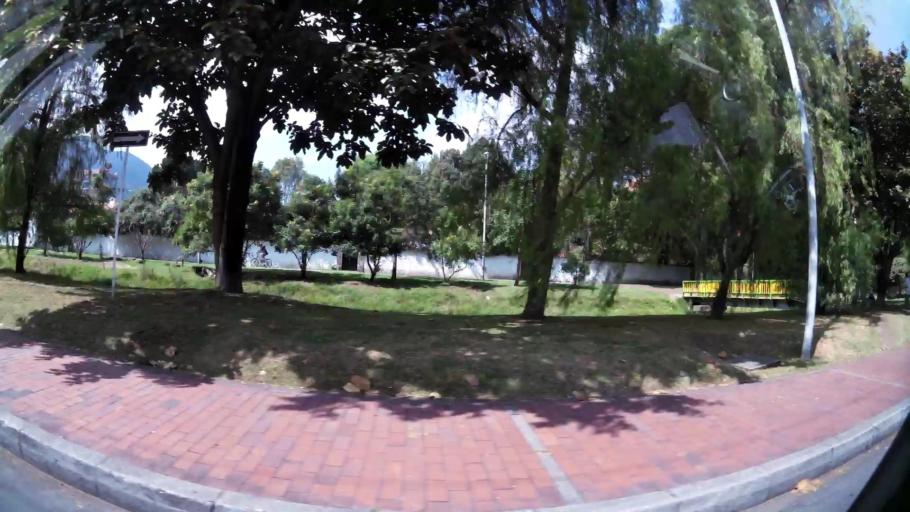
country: CO
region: Bogota D.C.
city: Barrio San Luis
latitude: 4.6878
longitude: -74.0366
